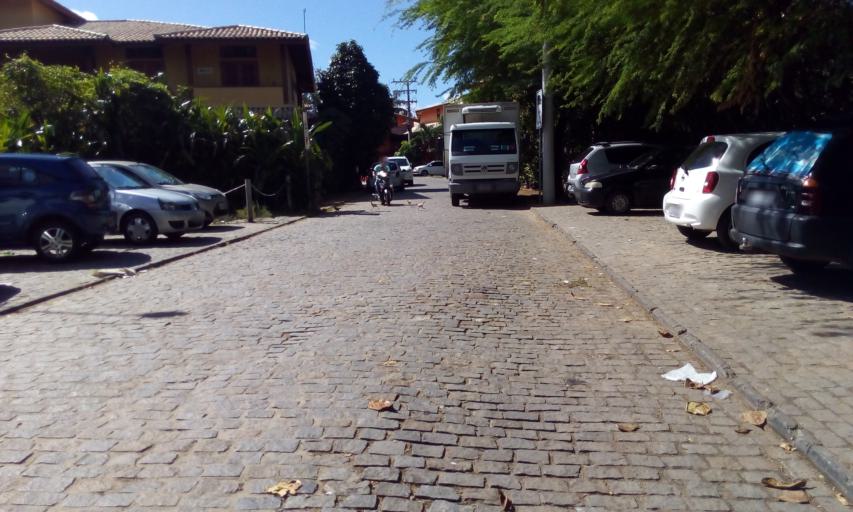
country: BR
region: Bahia
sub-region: Mata De Sao Joao
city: Mata de Sao Joao
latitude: -12.5766
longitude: -38.0070
